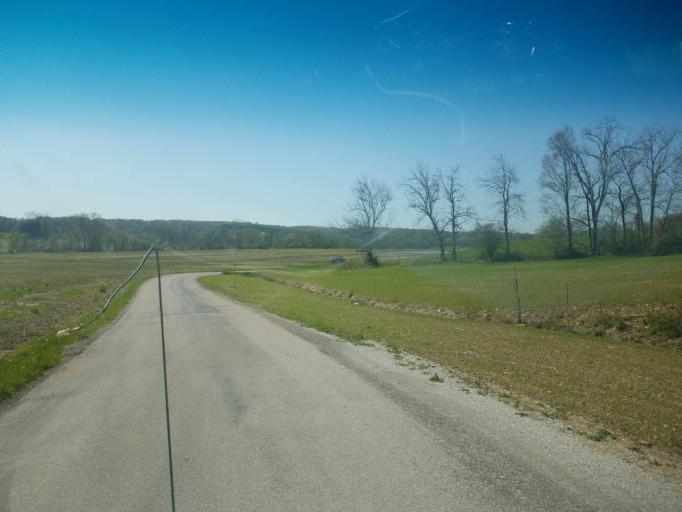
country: US
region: Ohio
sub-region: Medina County
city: Lodi
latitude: 40.9471
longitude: -82.0181
